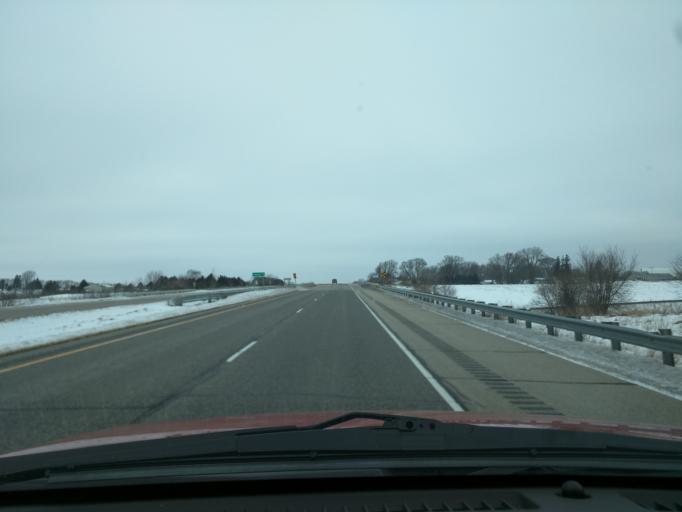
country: US
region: Minnesota
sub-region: Winona County
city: Winona
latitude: 43.9283
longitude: -91.6170
